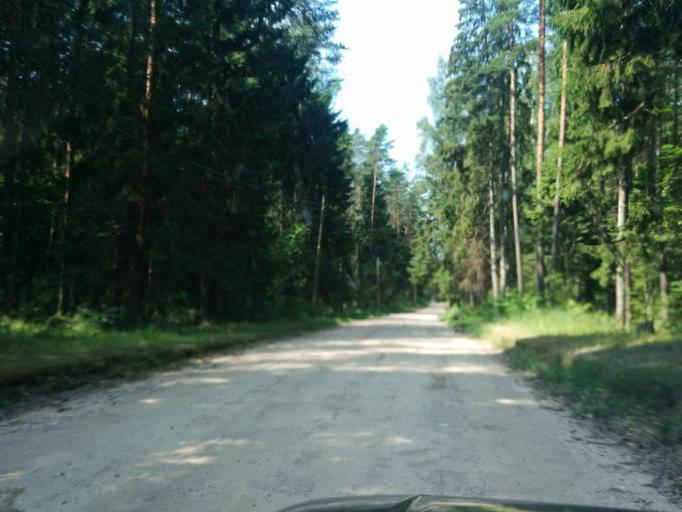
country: LV
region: Baldone
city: Baldone
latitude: 56.7426
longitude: 24.4305
